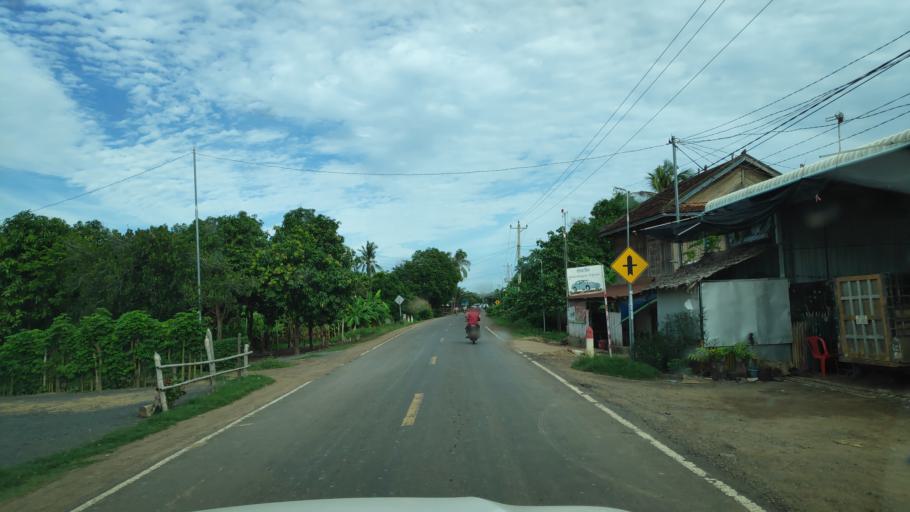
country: KH
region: Kampong Cham
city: Kampong Cham
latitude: 11.9470
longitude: 105.2436
